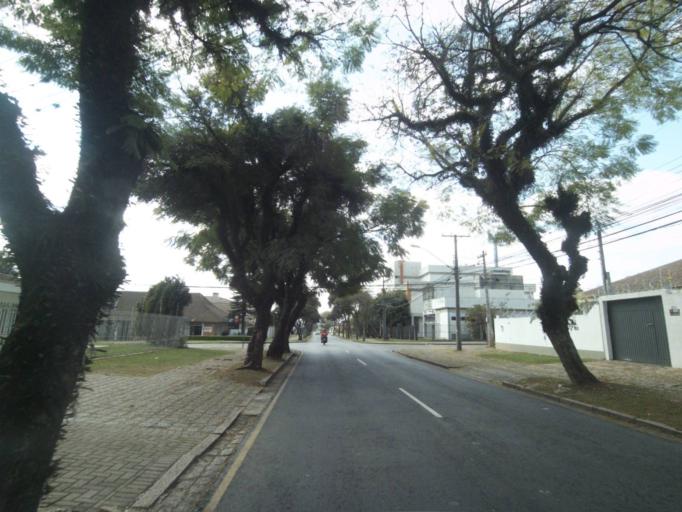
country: BR
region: Parana
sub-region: Curitiba
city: Curitiba
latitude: -25.4532
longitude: -49.2684
